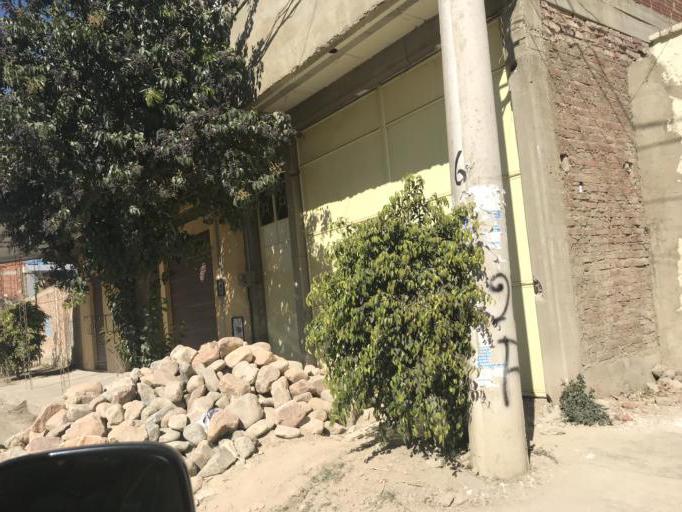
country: BO
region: Cochabamba
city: Punata
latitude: -17.5487
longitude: -65.8439
